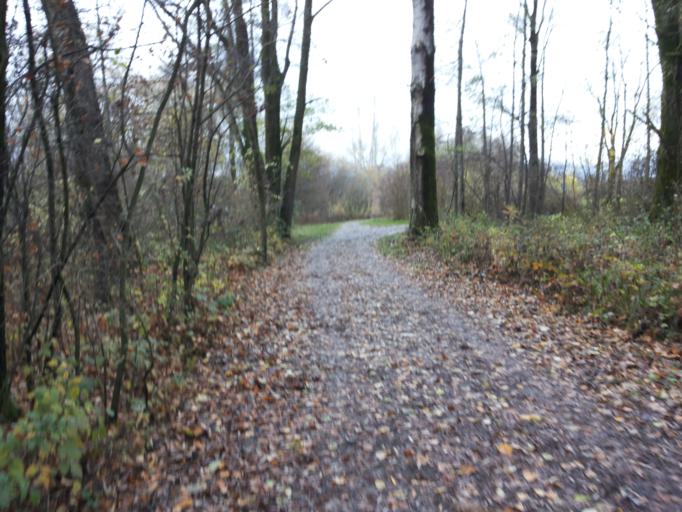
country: CH
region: Zug
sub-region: Zug
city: Cham
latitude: 47.1788
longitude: 8.4785
